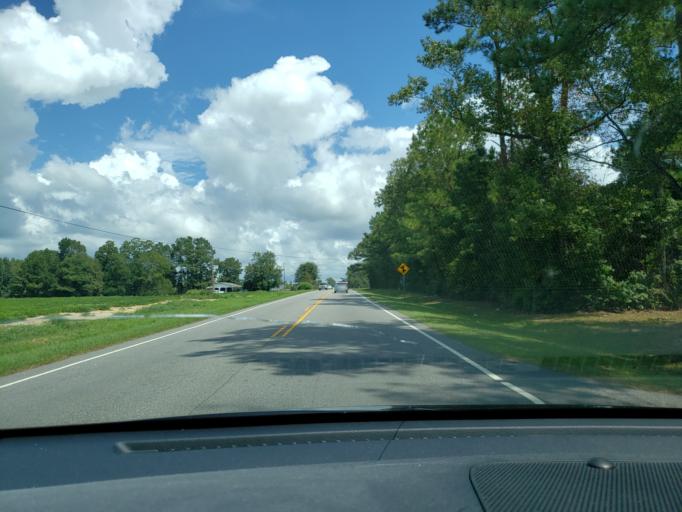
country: US
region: North Carolina
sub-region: Columbus County
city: Brunswick
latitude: 34.2539
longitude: -78.7501
